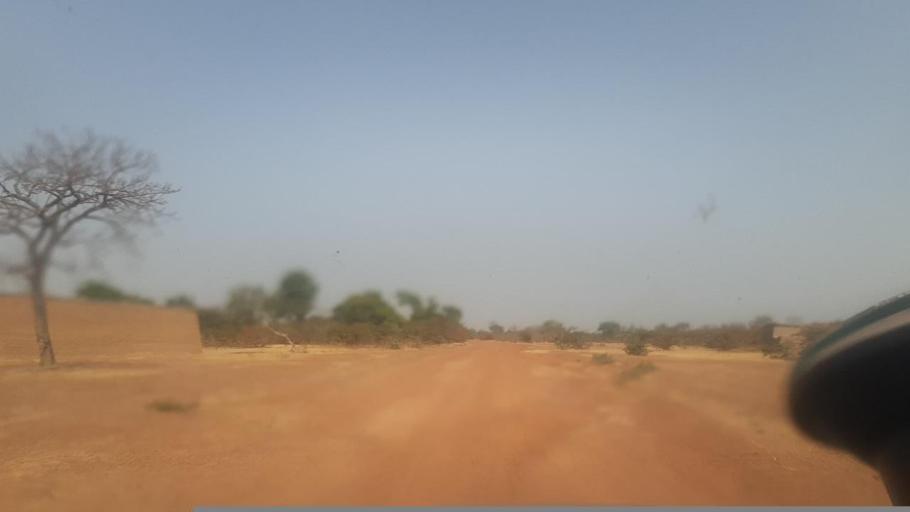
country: ML
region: Segou
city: Bla
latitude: 12.8574
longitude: -5.9716
